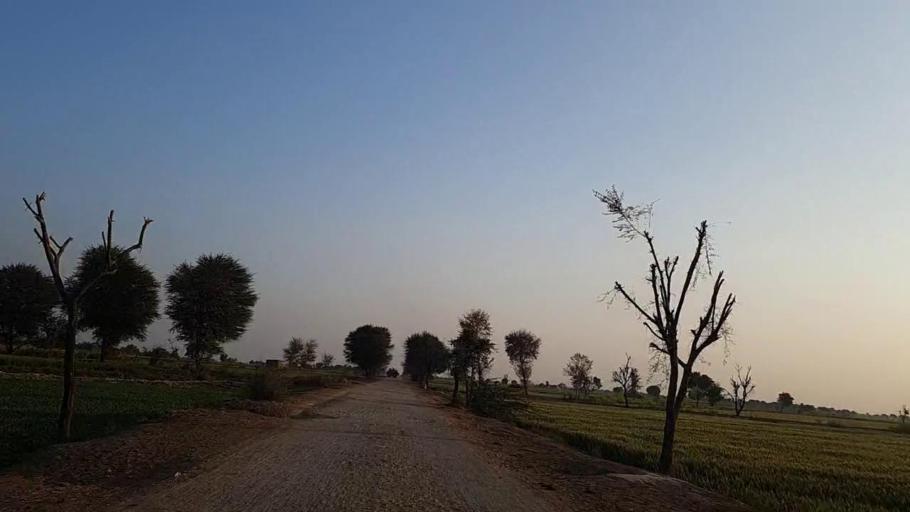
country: PK
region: Sindh
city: Shahdadpur
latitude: 26.0077
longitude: 68.4916
